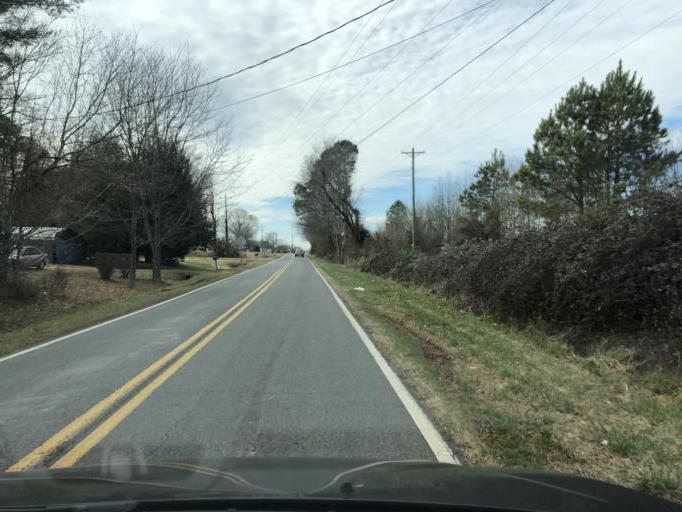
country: US
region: North Carolina
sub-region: Cleveland County
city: Shelby
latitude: 35.2542
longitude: -81.5002
